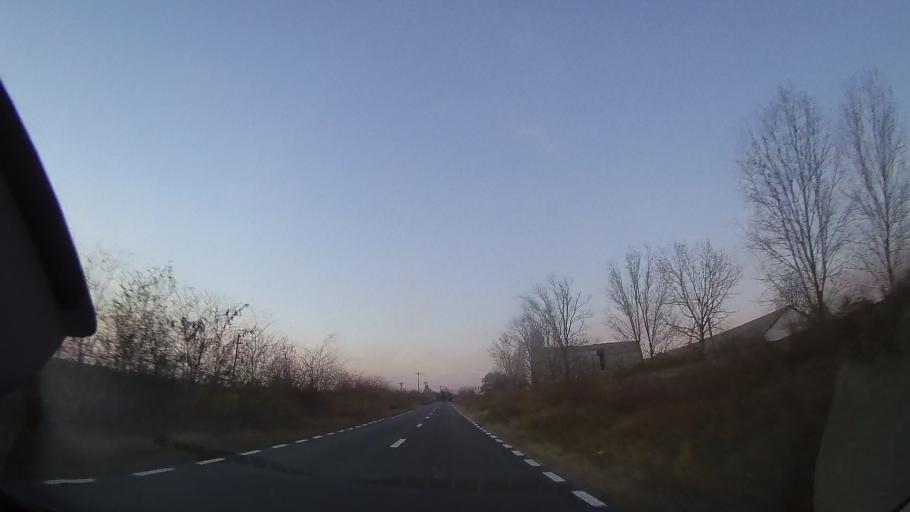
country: RO
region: Constanta
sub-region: Comuna Cobadin
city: Cobadin
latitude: 44.0498
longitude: 28.2495
